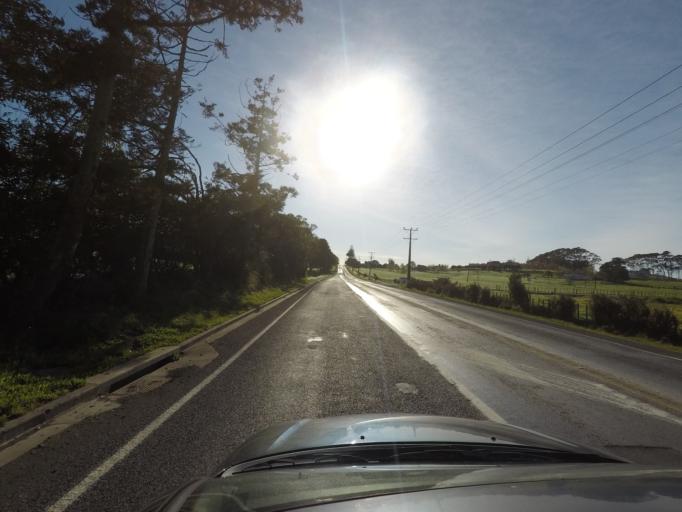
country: NZ
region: Auckland
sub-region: Auckland
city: Red Hill
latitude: -36.9982
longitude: 174.9701
